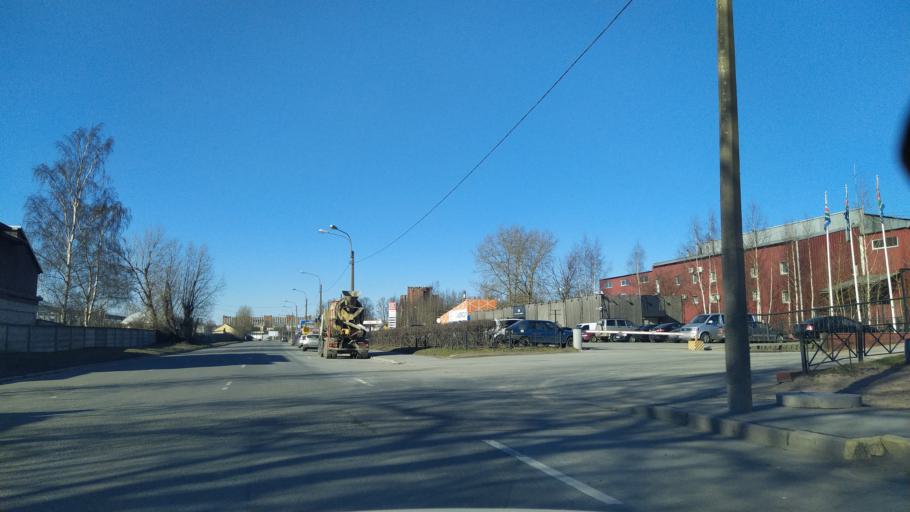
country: RU
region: St.-Petersburg
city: Centralniy
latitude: 59.9076
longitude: 30.3777
